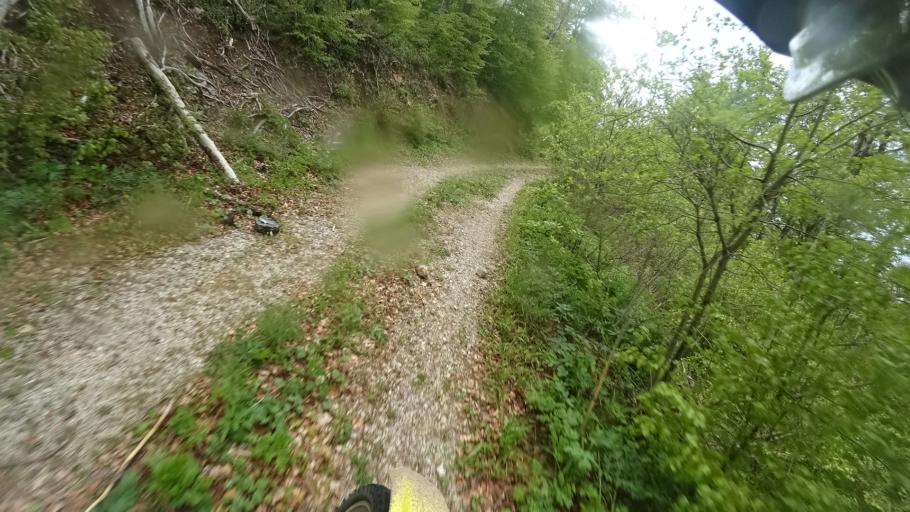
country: BA
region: Federation of Bosnia and Herzegovina
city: Orasac
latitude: 44.5743
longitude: 15.8724
